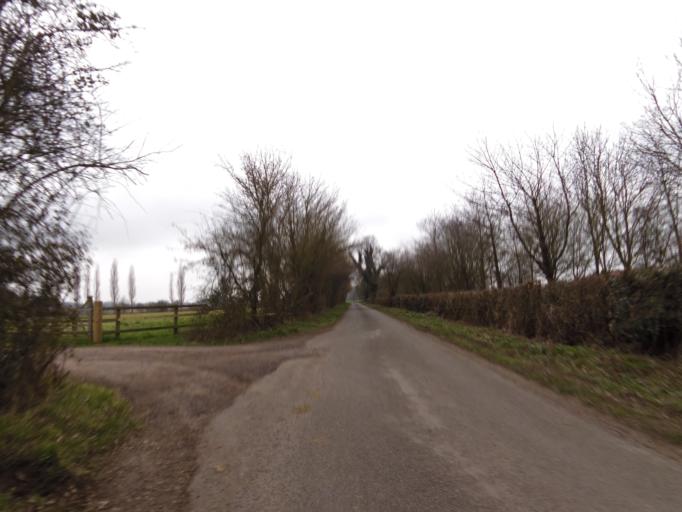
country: GB
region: England
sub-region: Suffolk
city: Framlingham
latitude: 52.1950
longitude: 1.3232
